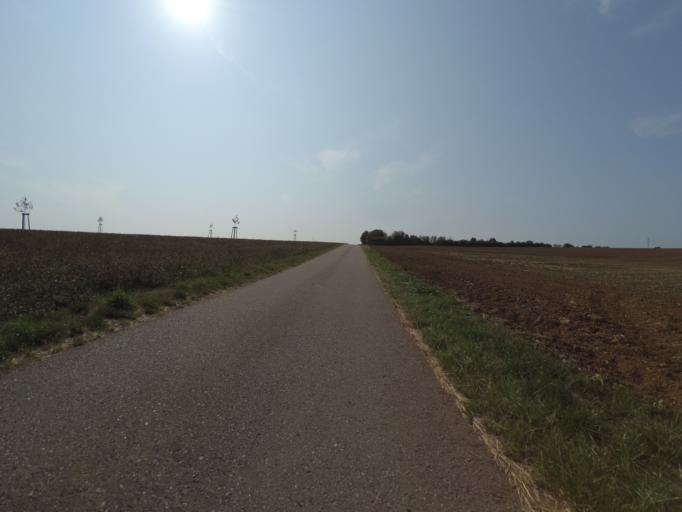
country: DE
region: Saarland
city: Perl
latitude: 49.4836
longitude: 6.4412
